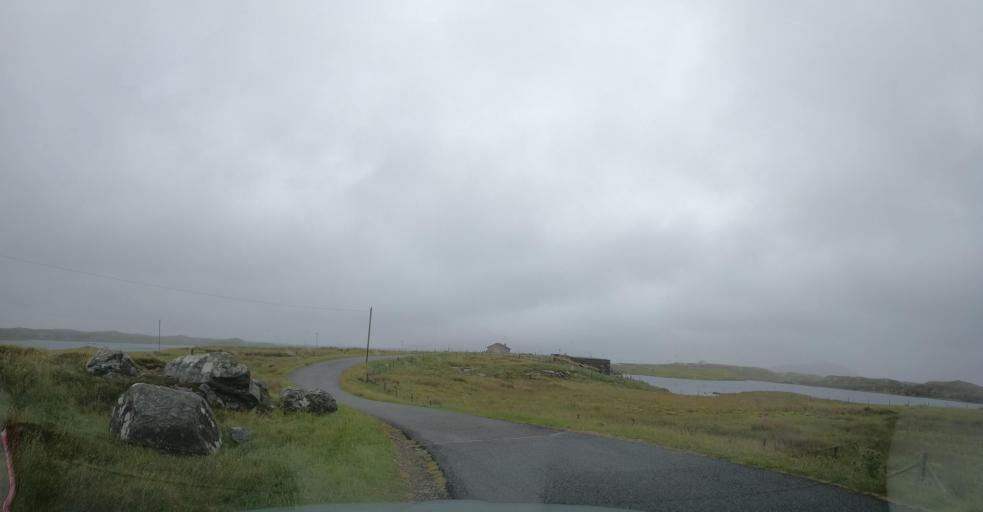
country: GB
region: Scotland
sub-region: Eilean Siar
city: Isle of North Uist
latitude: 57.5505
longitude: -7.2186
